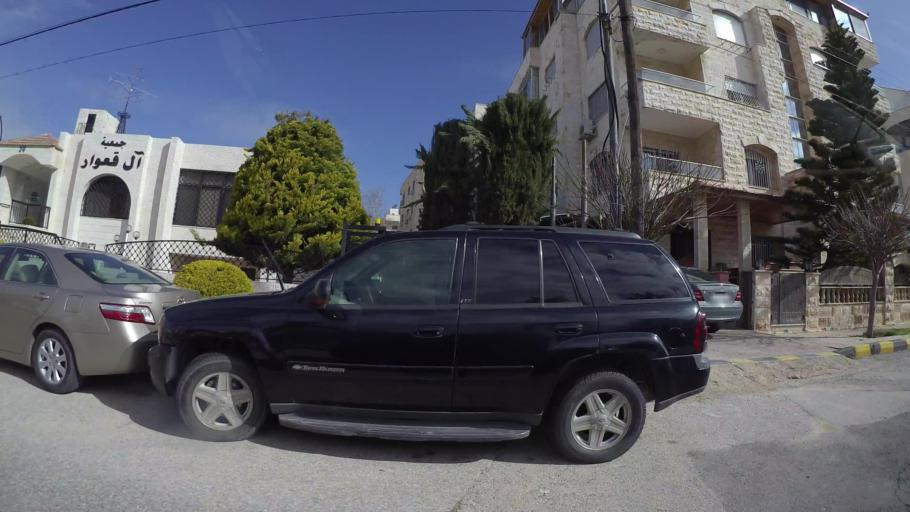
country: JO
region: Amman
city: Wadi as Sir
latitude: 31.9495
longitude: 35.8472
